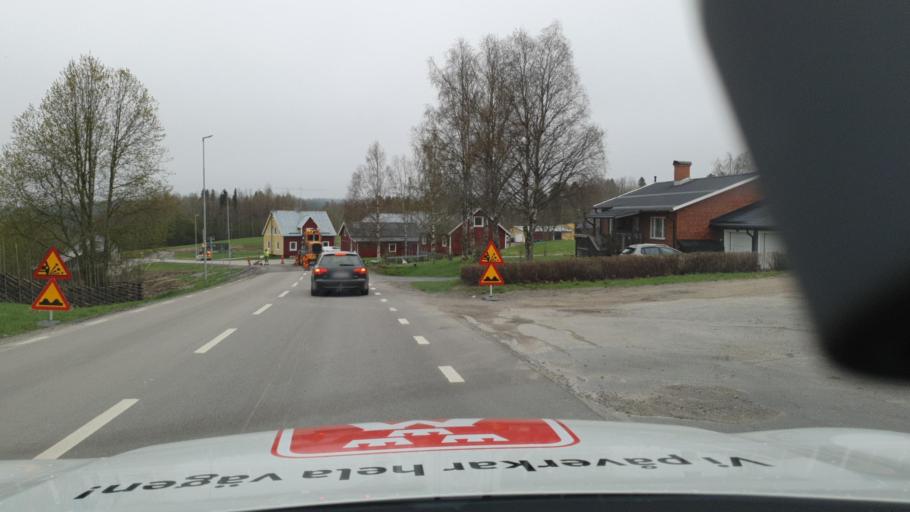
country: SE
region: Vaesterbotten
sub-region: Vannas Kommun
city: Vaennaes
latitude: 63.7690
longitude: 19.6218
